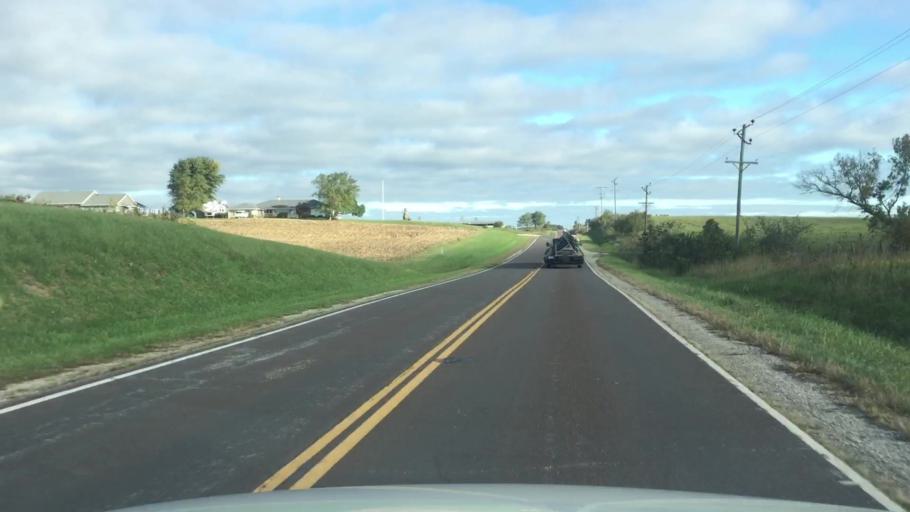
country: US
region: Missouri
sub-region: Howard County
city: New Franklin
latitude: 39.0690
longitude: -92.7460
